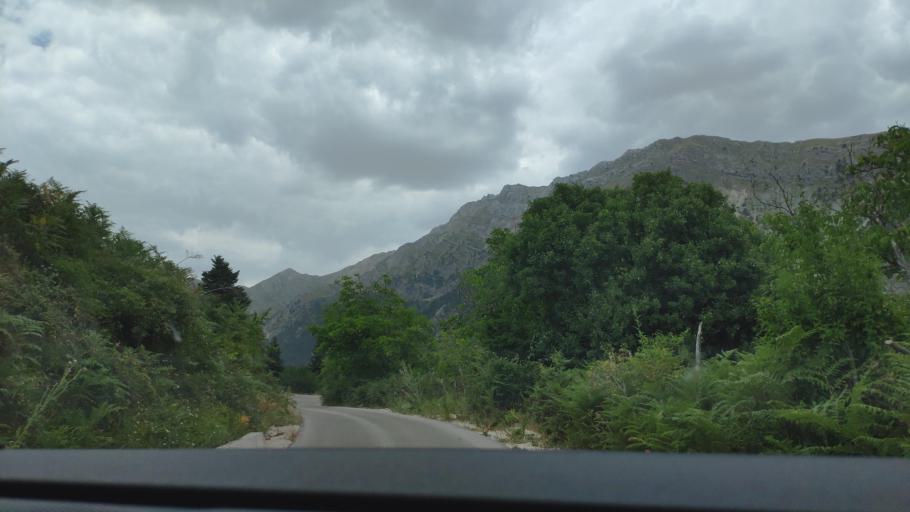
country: GR
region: Epirus
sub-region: Nomos Artas
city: Voulgareli
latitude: 39.4401
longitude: 21.2023
